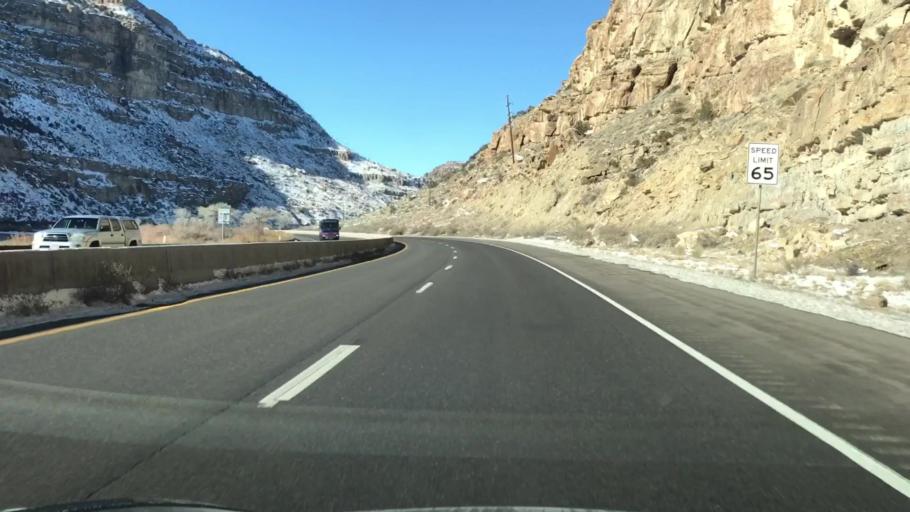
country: US
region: Colorado
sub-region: Mesa County
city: Palisade
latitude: 39.2292
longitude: -108.2646
